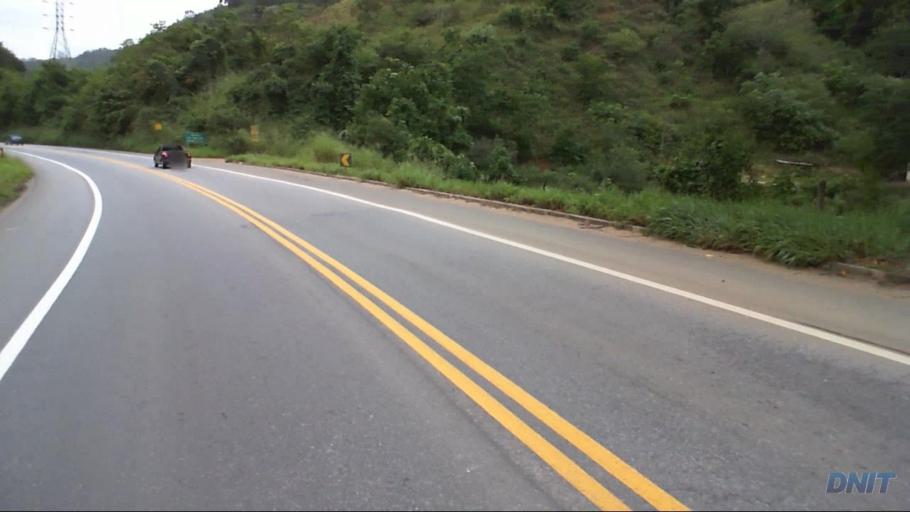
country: BR
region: Minas Gerais
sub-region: Timoteo
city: Timoteo
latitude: -19.5720
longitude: -42.7135
